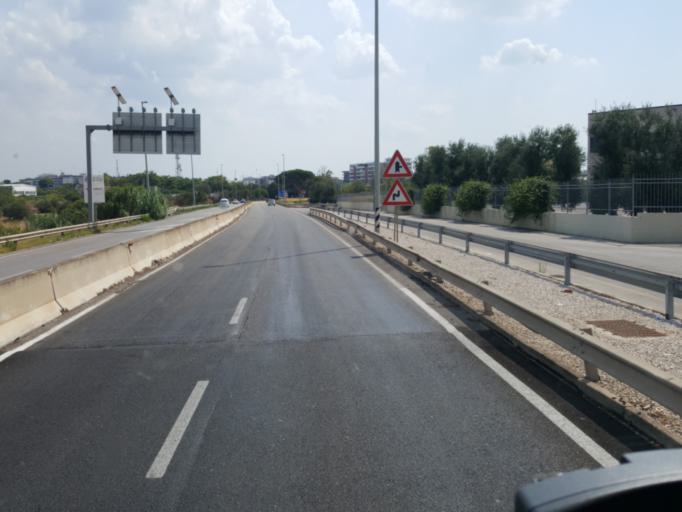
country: IT
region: Apulia
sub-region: Provincia di Bari
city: Modugno
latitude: 41.0960
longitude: 16.7739
